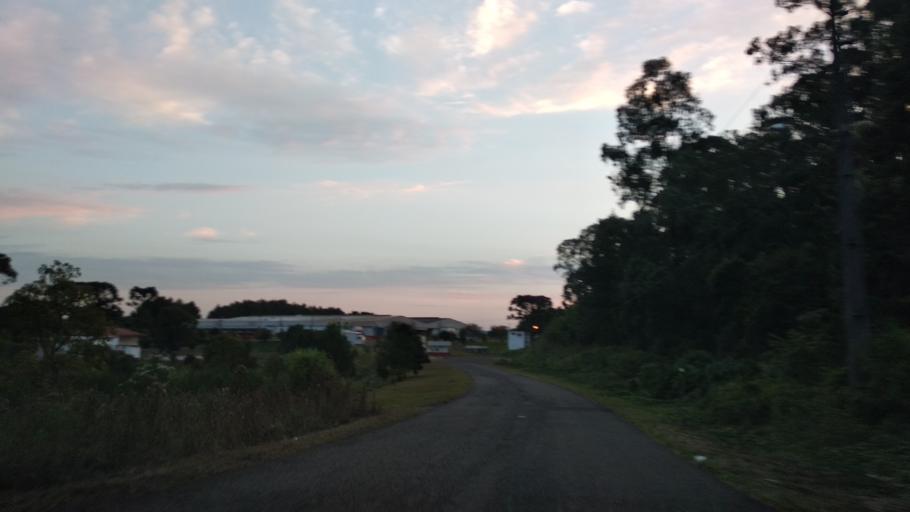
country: BR
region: Santa Catarina
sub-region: Videira
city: Videira
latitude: -26.9977
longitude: -51.1834
